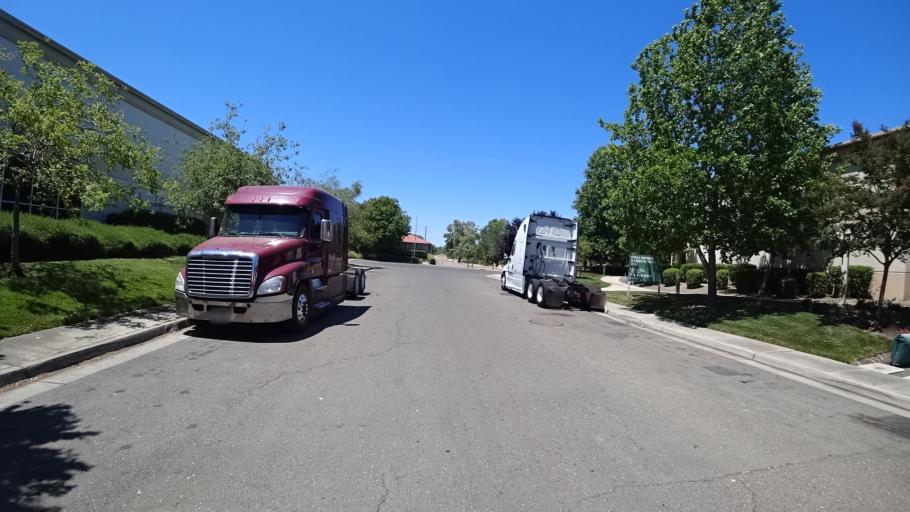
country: US
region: California
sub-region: Sacramento County
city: Rio Linda
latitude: 38.6505
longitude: -121.5045
